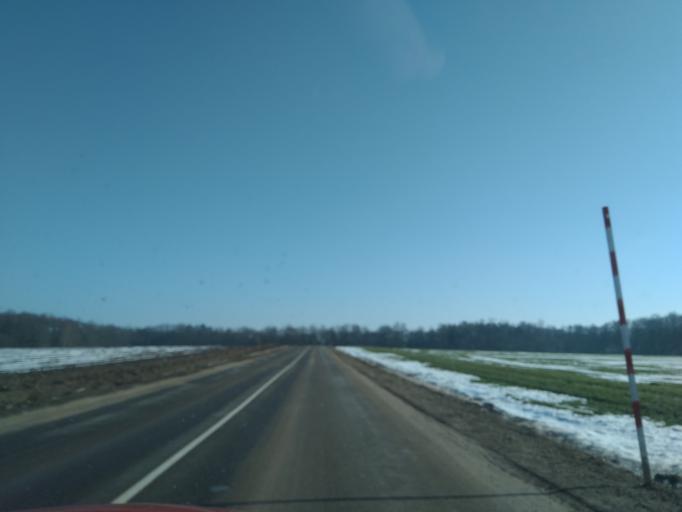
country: BY
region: Minsk
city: Nyasvizh
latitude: 53.2025
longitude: 26.6500
